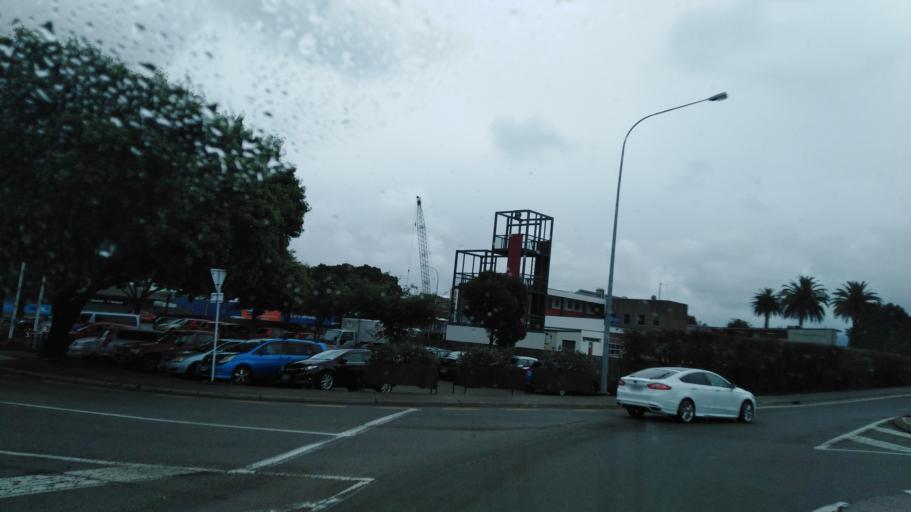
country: NZ
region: Marlborough
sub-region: Marlborough District
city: Blenheim
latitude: -41.5135
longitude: 173.9597
